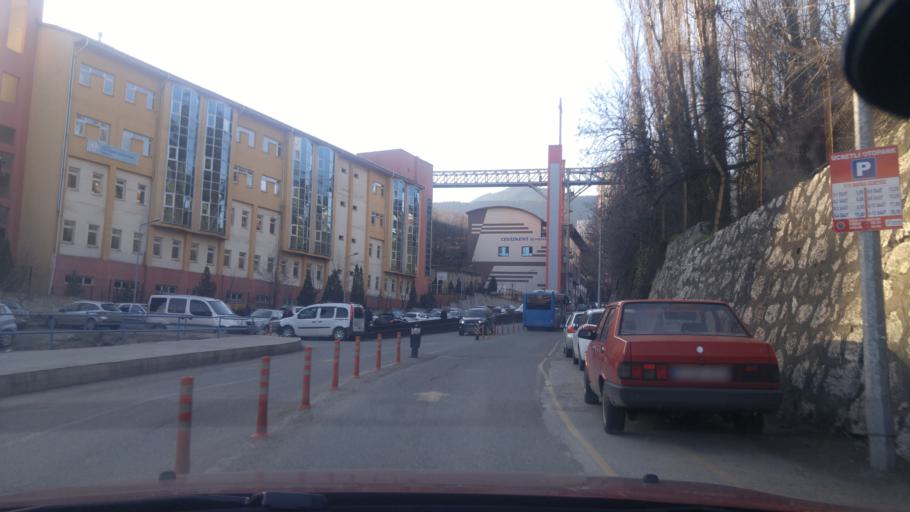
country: TR
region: Karabuk
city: Karabuk
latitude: 41.1984
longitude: 32.6174
